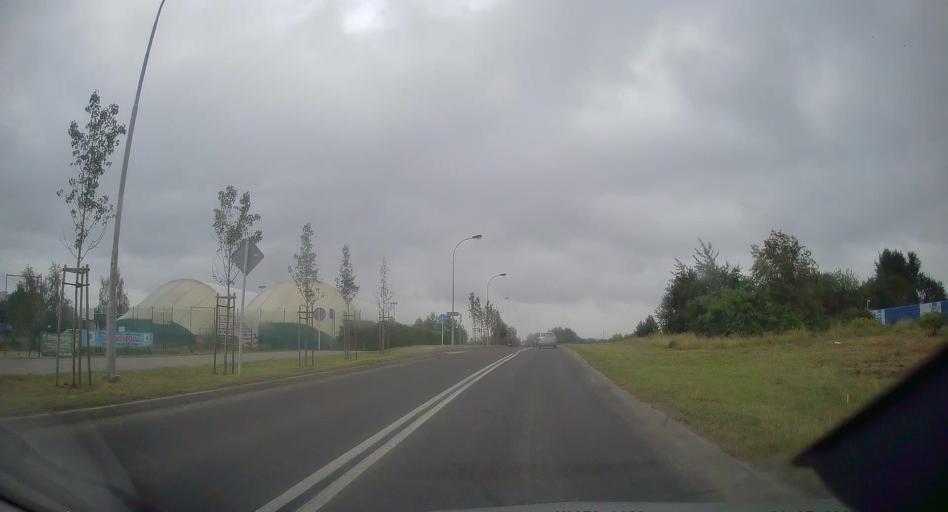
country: PL
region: Subcarpathian Voivodeship
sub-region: Rzeszow
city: Przybyszowka
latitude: 50.0437
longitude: 21.9557
